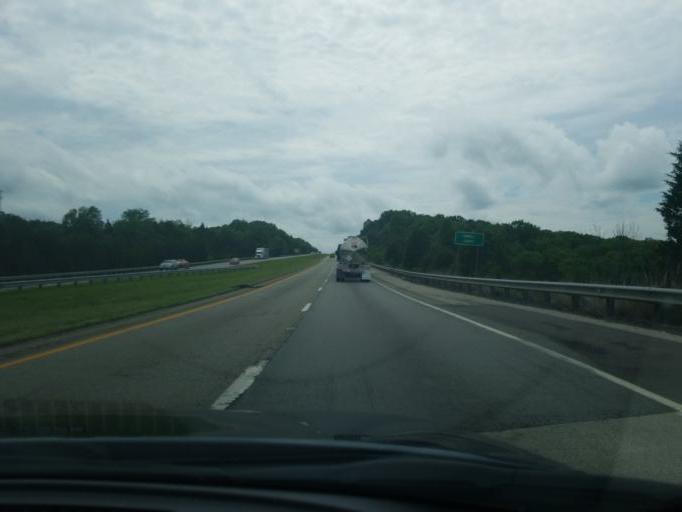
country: US
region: Kentucky
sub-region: Gallatin County
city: Warsaw
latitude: 38.6823
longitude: -84.9644
